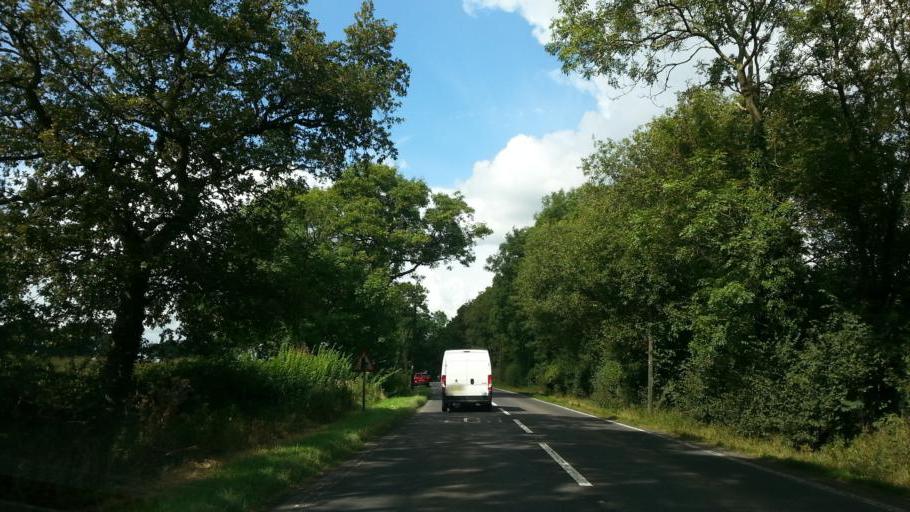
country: GB
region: England
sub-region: Nottinghamshire
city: Farnsfield
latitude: 53.1143
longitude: -0.9917
